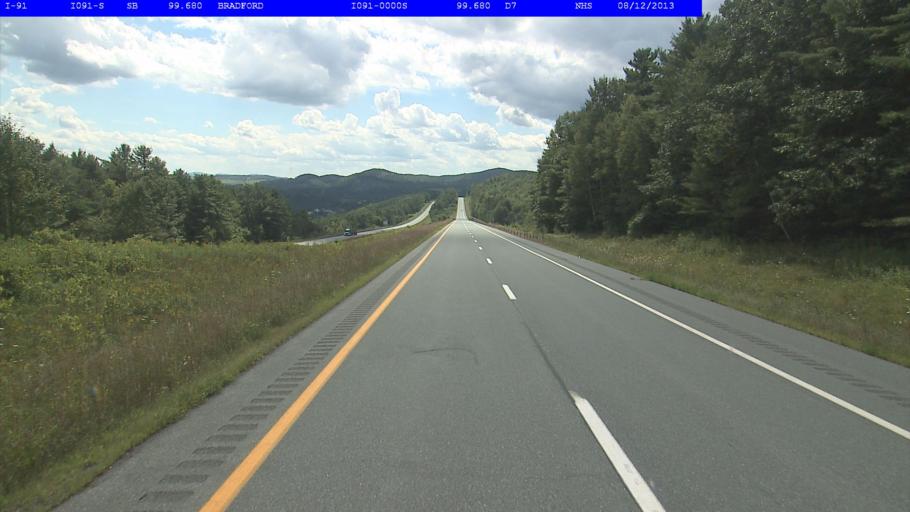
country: US
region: New Hampshire
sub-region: Grafton County
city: Haverhill
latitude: 44.0112
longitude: -72.1242
